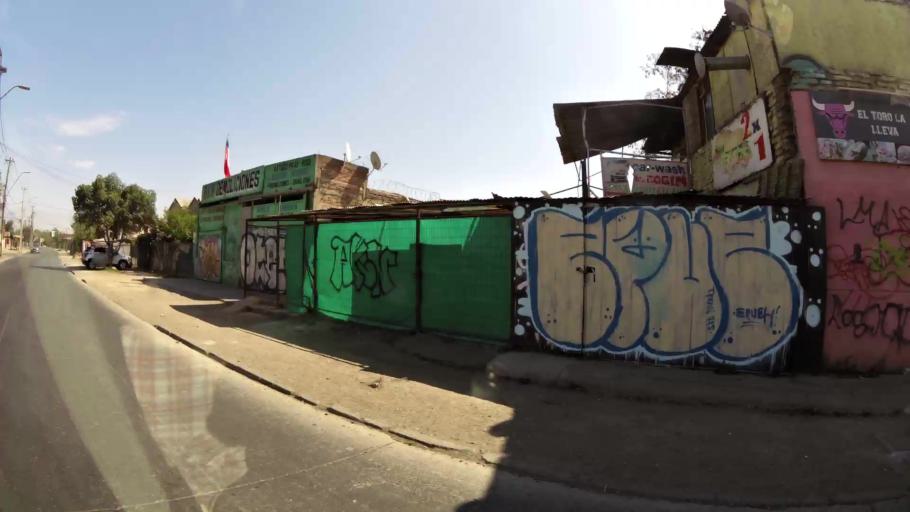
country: CL
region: Santiago Metropolitan
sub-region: Provincia de Santiago
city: Lo Prado
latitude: -33.4043
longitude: -70.7201
